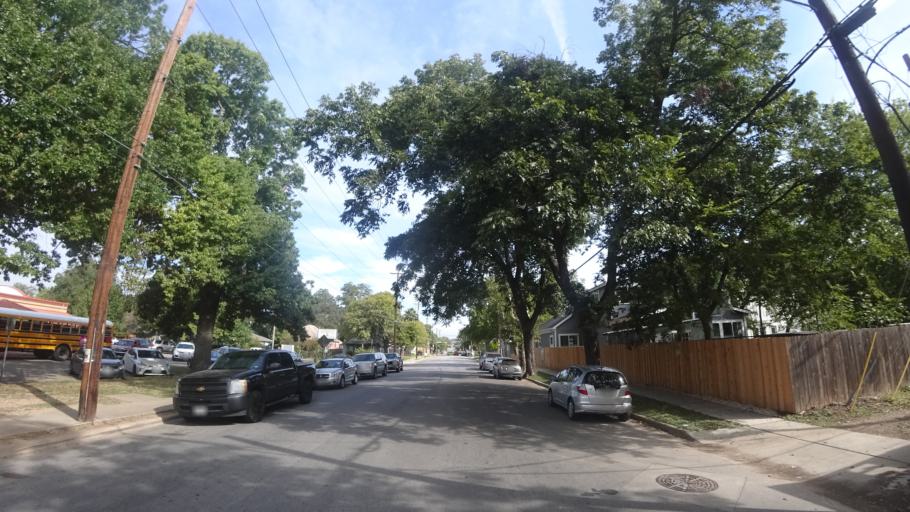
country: US
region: Texas
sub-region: Travis County
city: Austin
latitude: 30.2543
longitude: -97.7213
